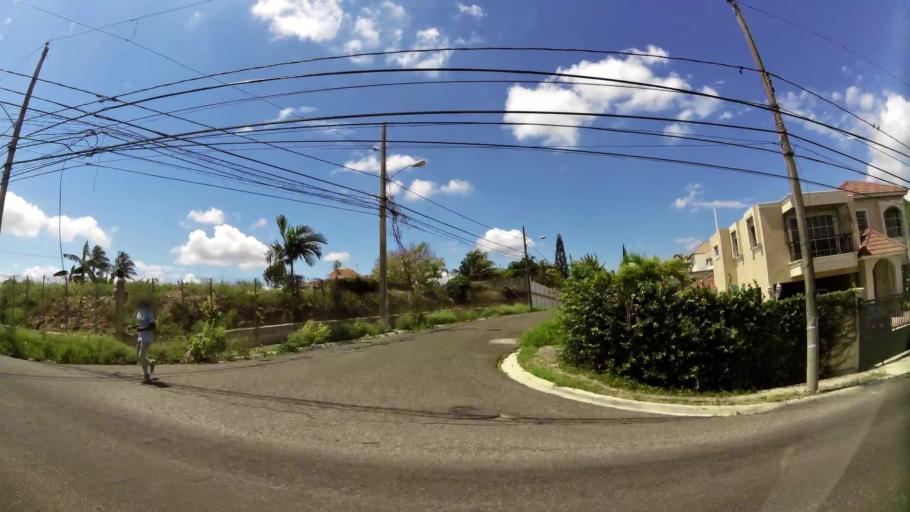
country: DO
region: Santiago
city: Santiago de los Caballeros
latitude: 19.4666
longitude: -70.6779
